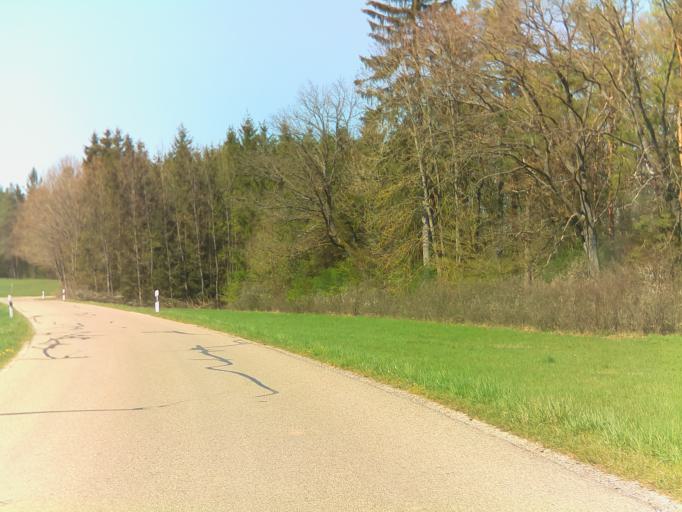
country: DE
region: Bavaria
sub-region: Upper Palatinate
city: Weigendorf
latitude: 49.4841
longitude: 11.5672
